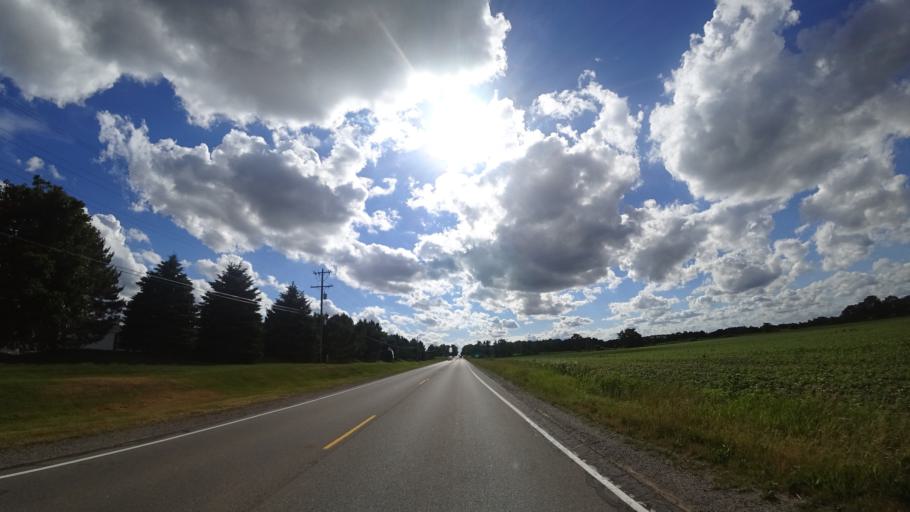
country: US
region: Michigan
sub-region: Ionia County
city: Portland
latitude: 42.8716
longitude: -84.9328
